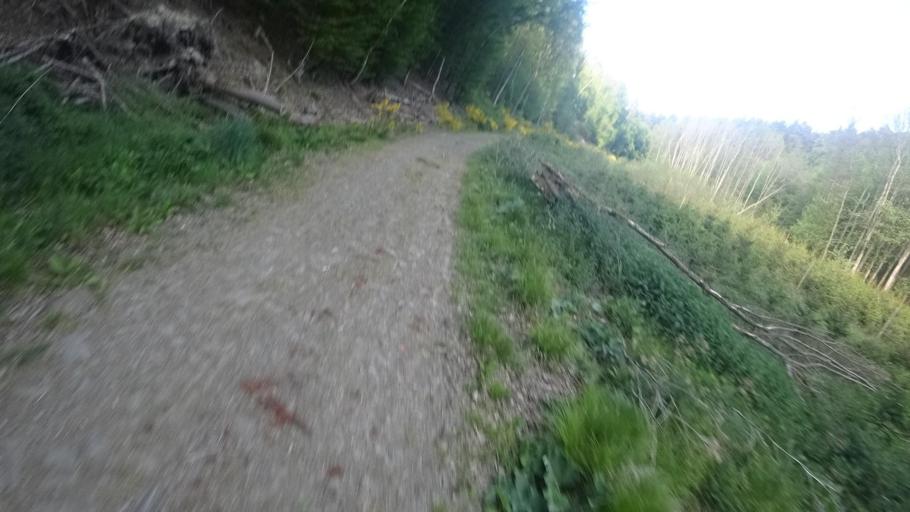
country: DE
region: Rheinland-Pfalz
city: Berg
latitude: 50.5283
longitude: 6.9666
